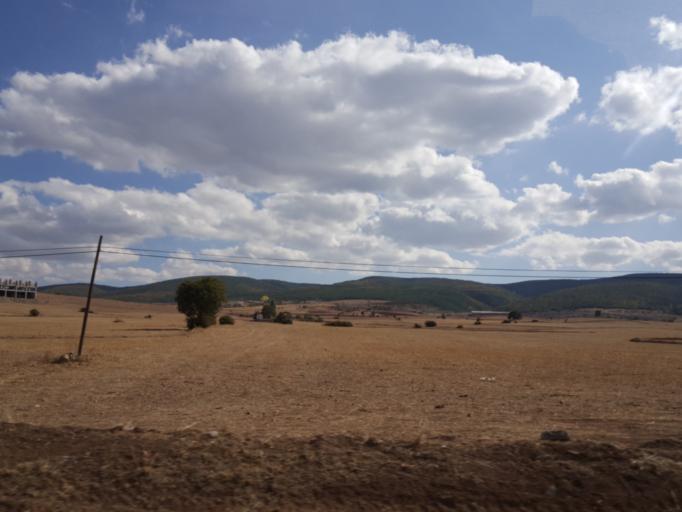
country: TR
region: Tokat
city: Yesilyurt
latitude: 40.0094
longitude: 36.1912
